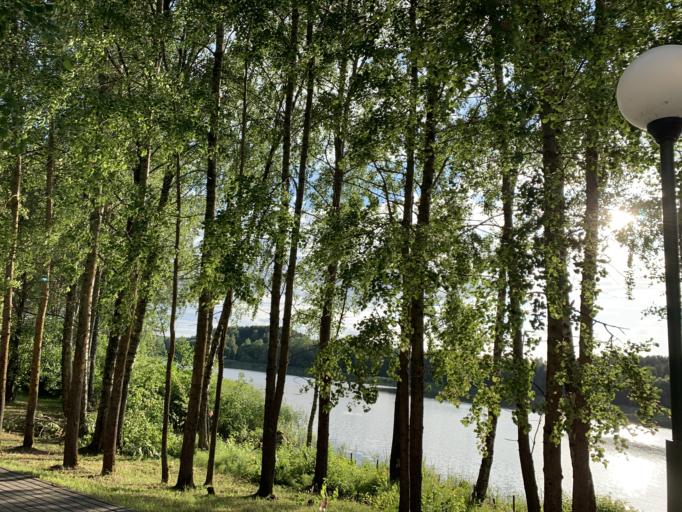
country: BY
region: Minsk
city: Khatsyezhyna
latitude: 53.9735
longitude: 27.3426
